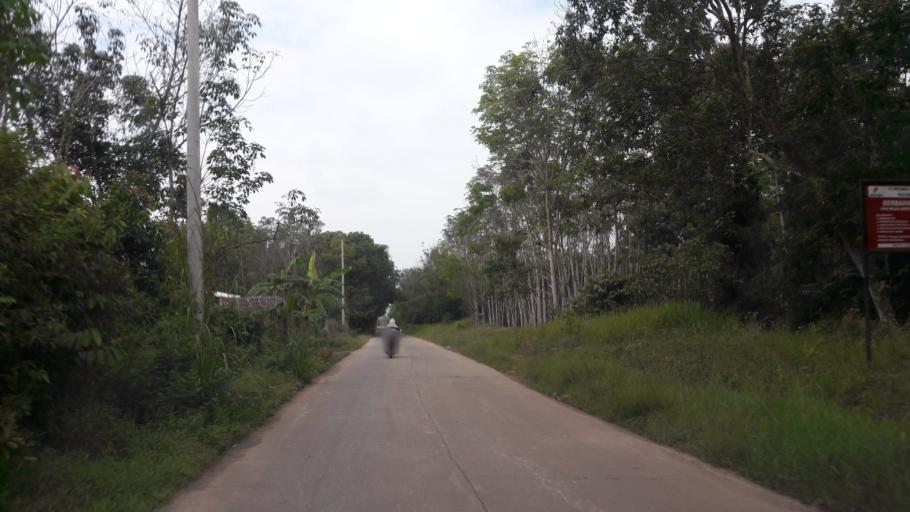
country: ID
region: South Sumatra
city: Gunungmenang
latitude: -3.2484
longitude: 104.1388
